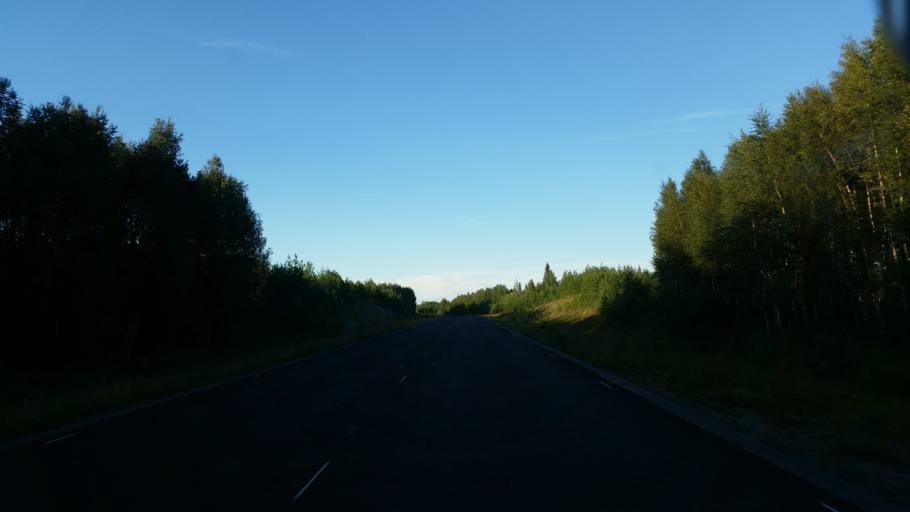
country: SE
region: Vaesterbotten
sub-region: Dorotea Kommun
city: Dorotea
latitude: 64.3261
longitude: 16.6250
